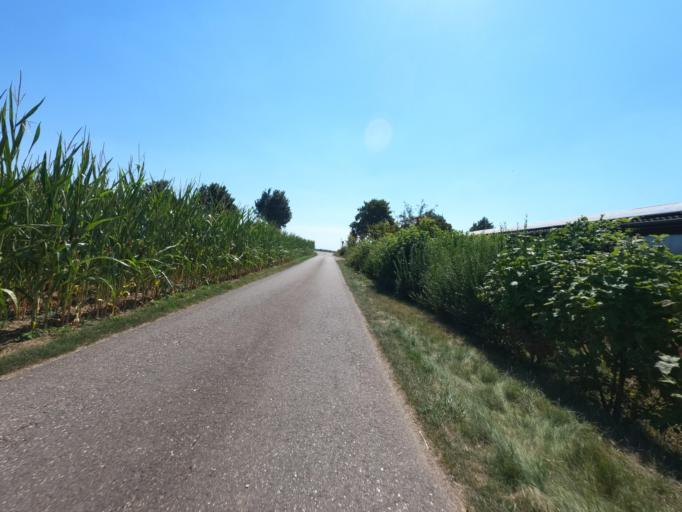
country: DE
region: North Rhine-Westphalia
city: Huckelhoven
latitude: 51.0934
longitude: 6.2542
